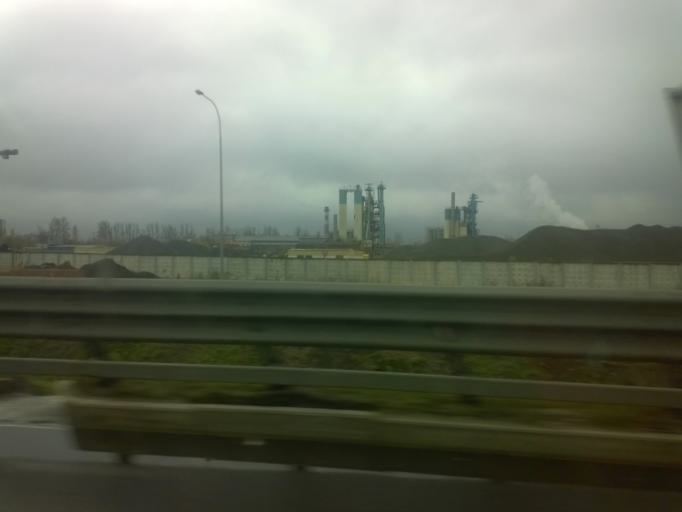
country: RU
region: St.-Petersburg
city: Kupchino
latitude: 59.8157
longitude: 30.3123
